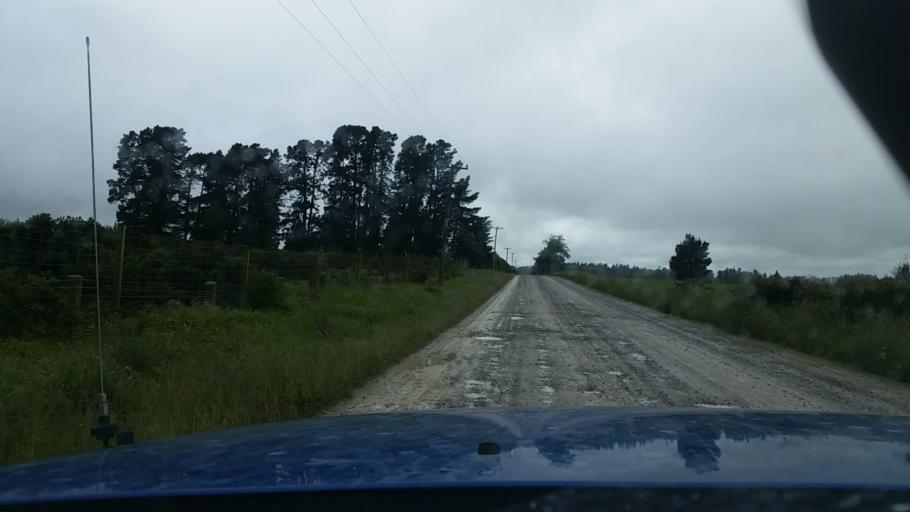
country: NZ
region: Canterbury
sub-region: Ashburton District
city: Methven
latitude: -43.6080
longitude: 171.4723
